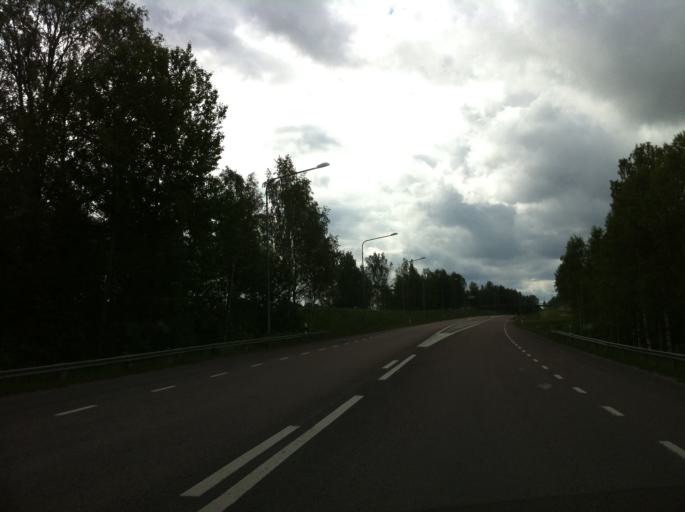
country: SE
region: Vaermland
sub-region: Sunne Kommun
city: Sunne
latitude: 59.8348
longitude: 13.1290
